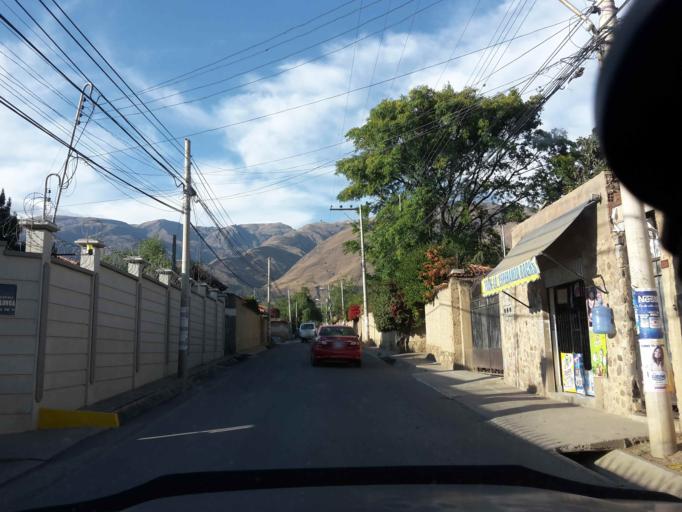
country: BO
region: Cochabamba
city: Cochabamba
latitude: -17.3434
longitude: -66.2057
